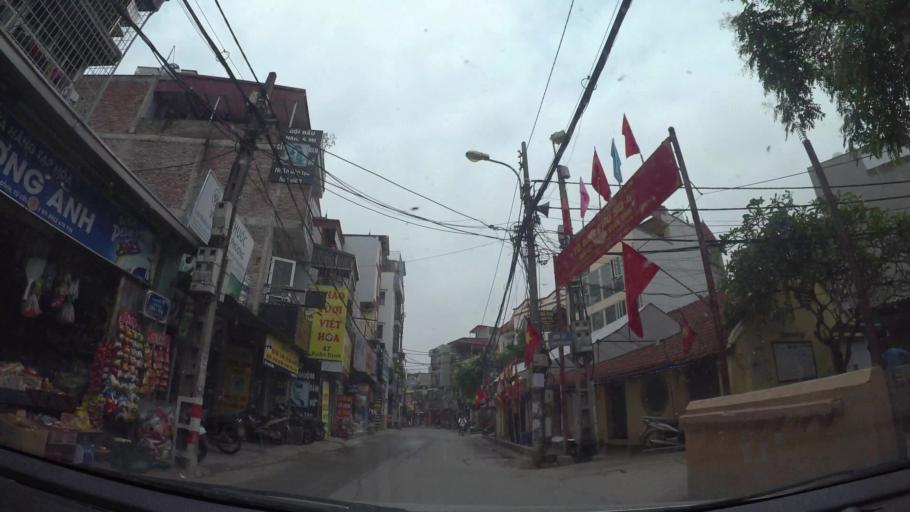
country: VN
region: Ha Noi
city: Tay Ho
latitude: 21.0699
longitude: 105.8016
